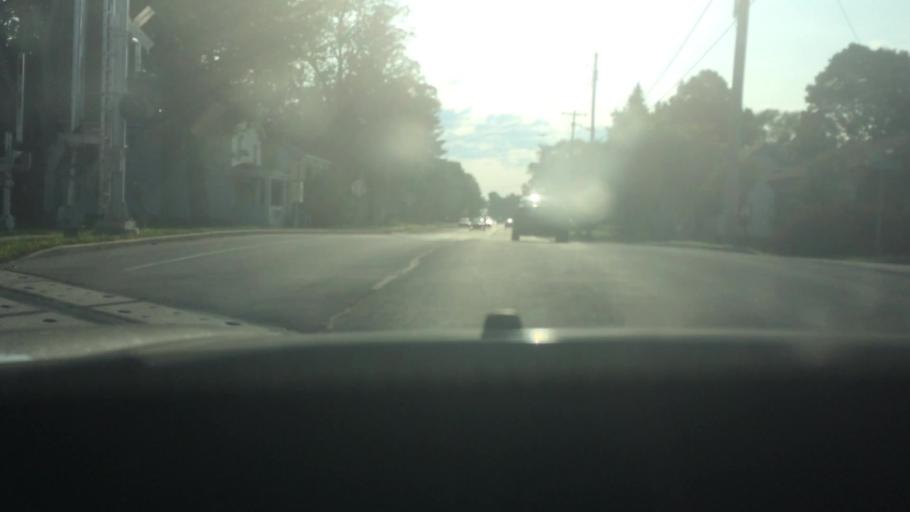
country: US
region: New York
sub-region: St. Lawrence County
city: Canton
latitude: 44.5959
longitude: -75.1650
